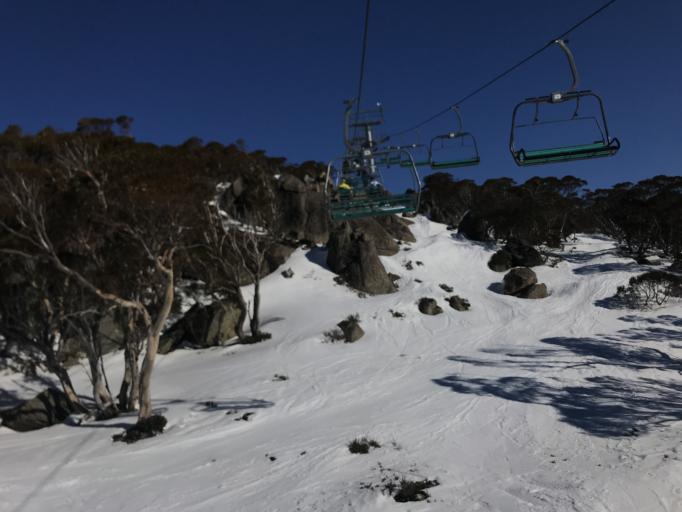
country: AU
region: New South Wales
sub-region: Snowy River
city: Jindabyne
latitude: -36.3845
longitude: 148.3957
